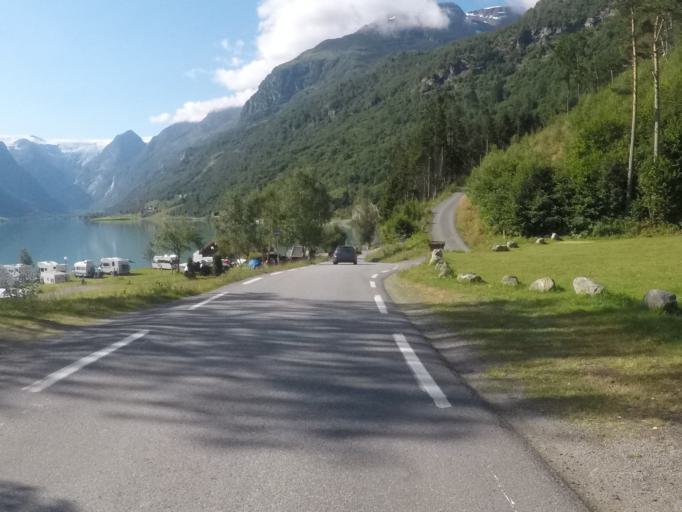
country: NO
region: Sogn og Fjordane
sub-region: Stryn
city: Stryn
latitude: 61.7401
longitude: 6.7902
